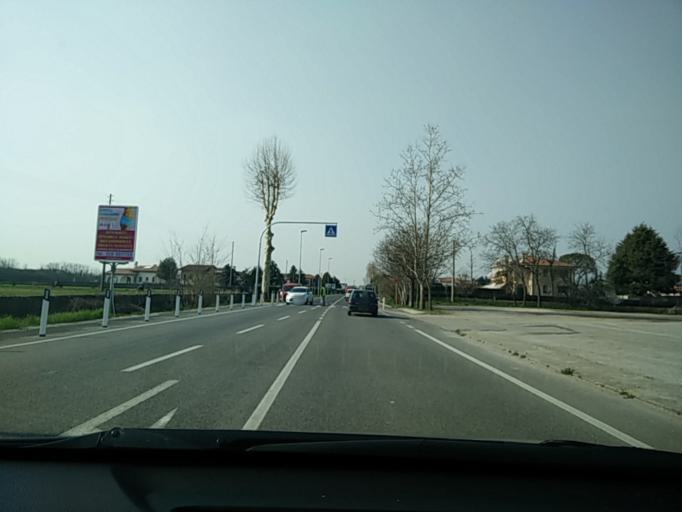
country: IT
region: Veneto
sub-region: Provincia di Treviso
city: Castagnole
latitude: 45.6978
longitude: 12.1854
